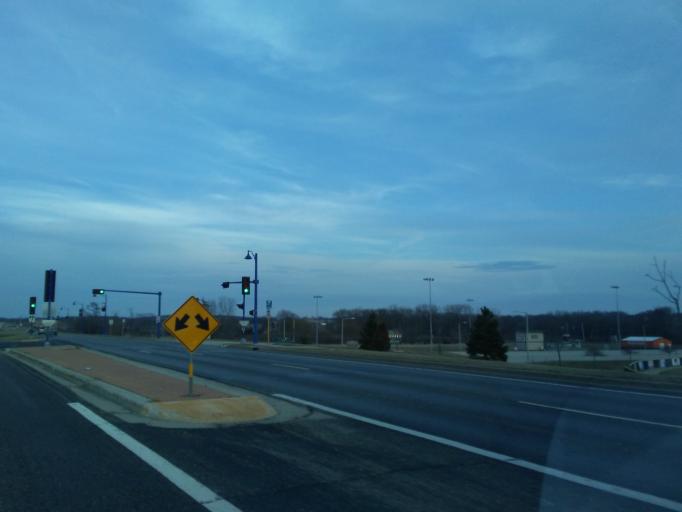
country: US
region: Wisconsin
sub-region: Dane County
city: Verona
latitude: 42.9938
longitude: -89.5197
